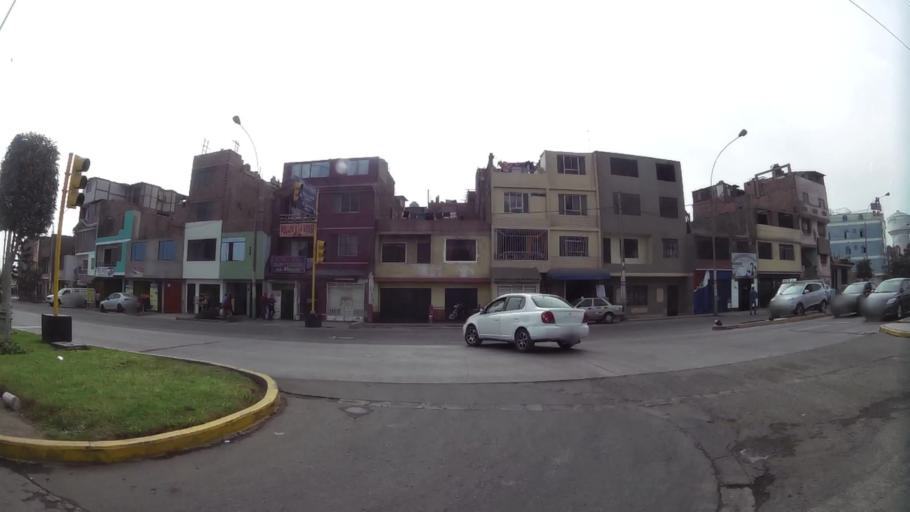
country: PE
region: Callao
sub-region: Callao
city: Callao
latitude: -12.0356
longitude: -77.0973
